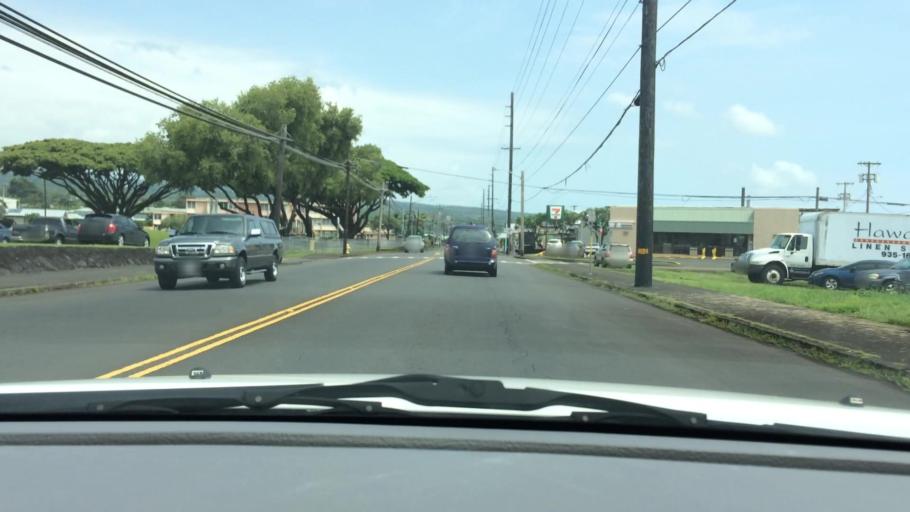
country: US
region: Hawaii
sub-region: Hawaii County
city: Hilo
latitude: 19.7148
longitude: -155.0824
